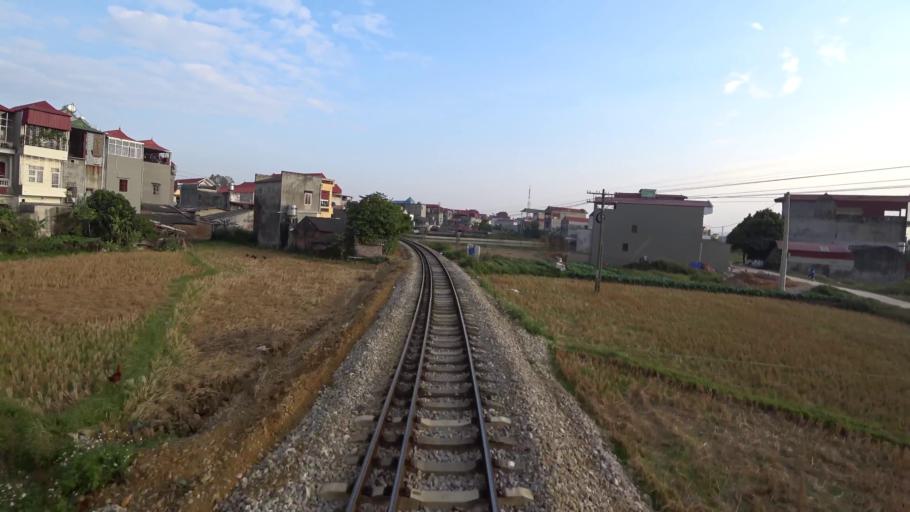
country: VN
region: Lang Son
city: Thi Tran Cao Loc
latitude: 21.8791
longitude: 106.7502
